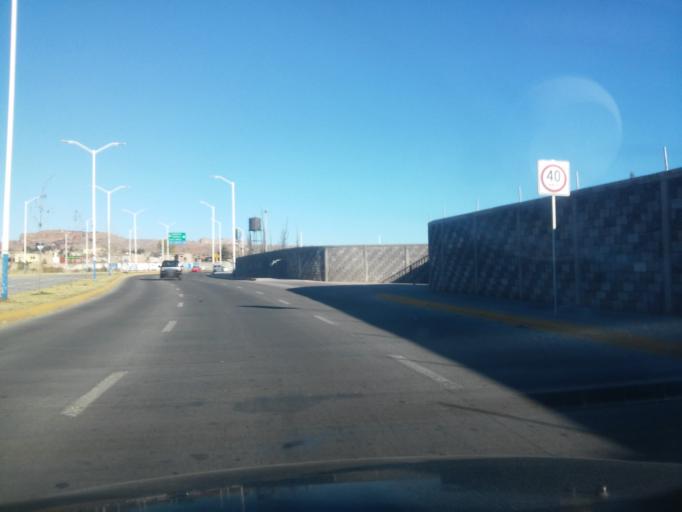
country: MX
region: Durango
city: Victoria de Durango
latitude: 24.0359
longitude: -104.6600
